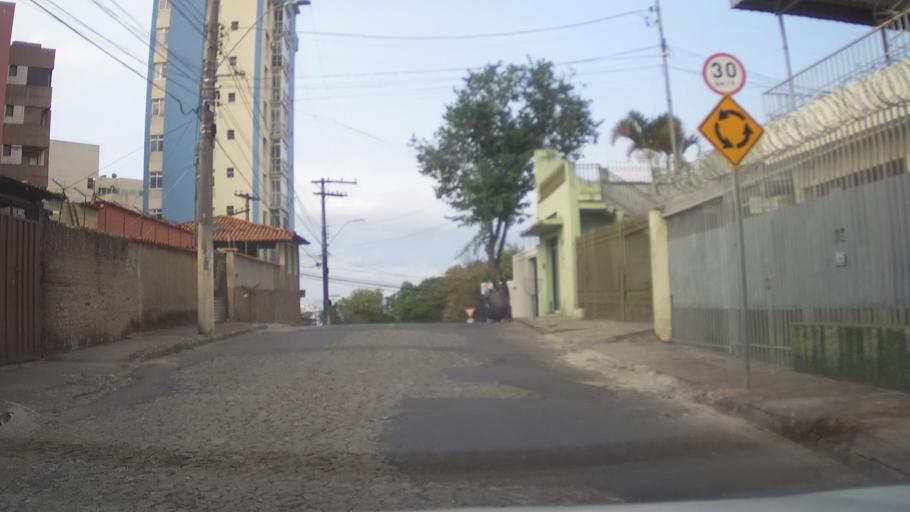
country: BR
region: Minas Gerais
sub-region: Belo Horizonte
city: Belo Horizonte
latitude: -19.8963
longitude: -43.9291
